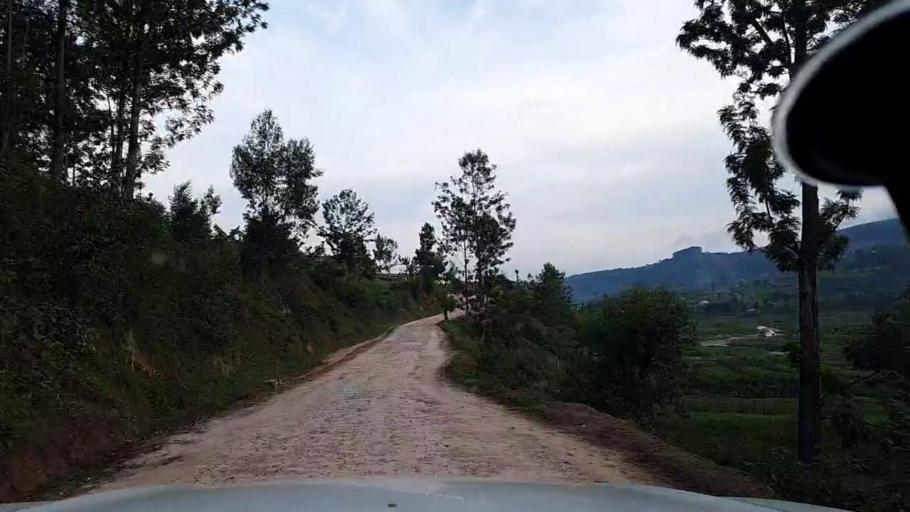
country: RW
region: Southern Province
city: Nyanza
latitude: -2.2199
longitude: 29.6454
